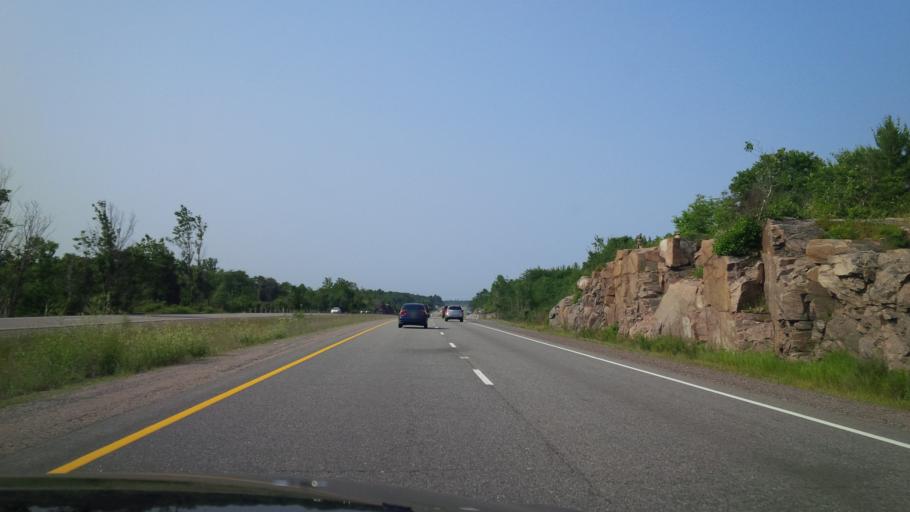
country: CA
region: Ontario
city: Gravenhurst
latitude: 44.9622
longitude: -79.3253
